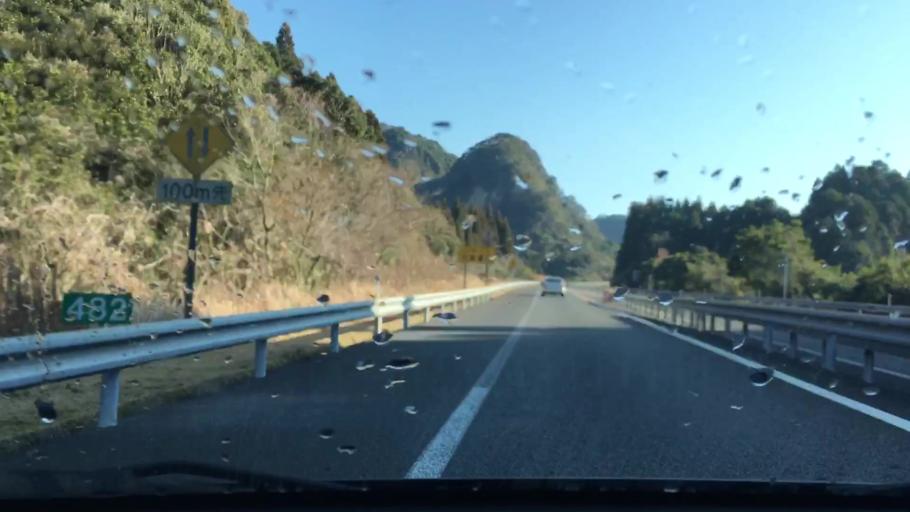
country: JP
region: Kagoshima
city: Kokubu-matsuki
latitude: 31.7447
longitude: 130.8071
